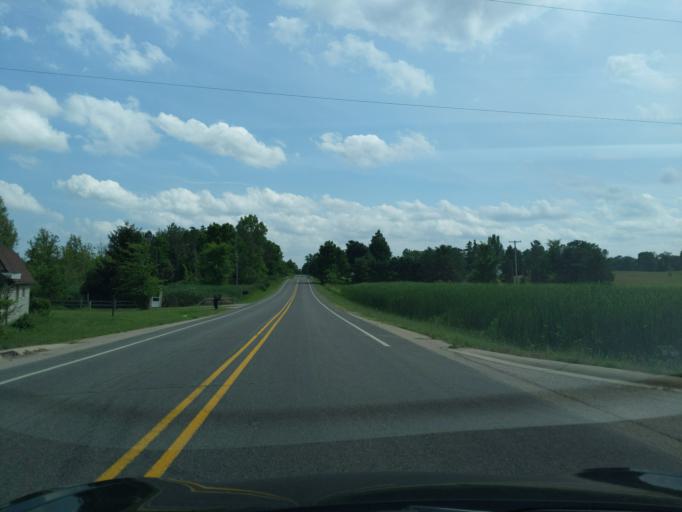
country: US
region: Michigan
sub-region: Eaton County
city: Dimondale
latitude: 42.5968
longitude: -84.6025
